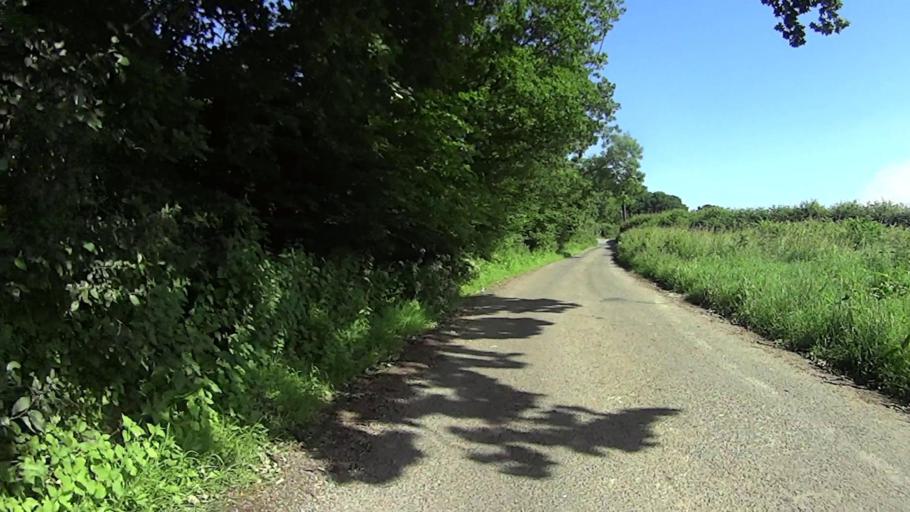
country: GB
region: England
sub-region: Surrey
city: Newdigate
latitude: 51.1117
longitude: -0.2902
